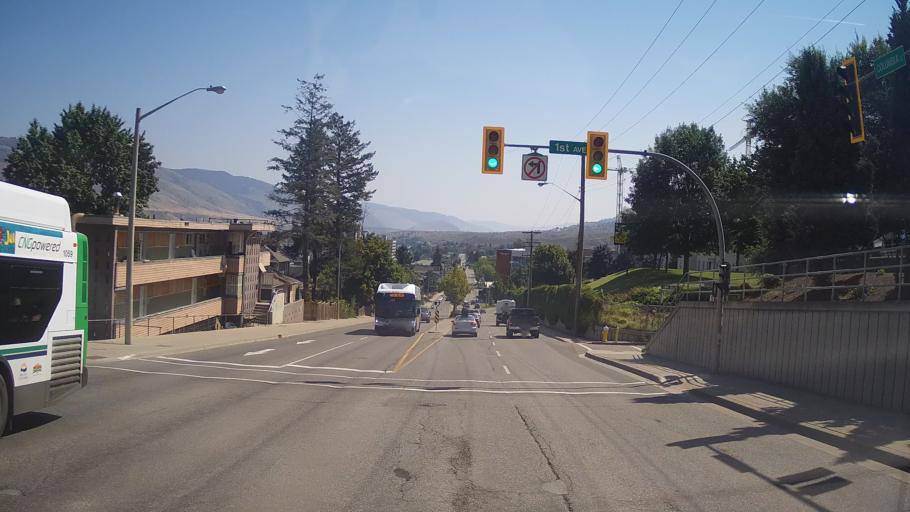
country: CA
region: British Columbia
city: Kamloops
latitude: 50.6714
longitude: -120.3392
